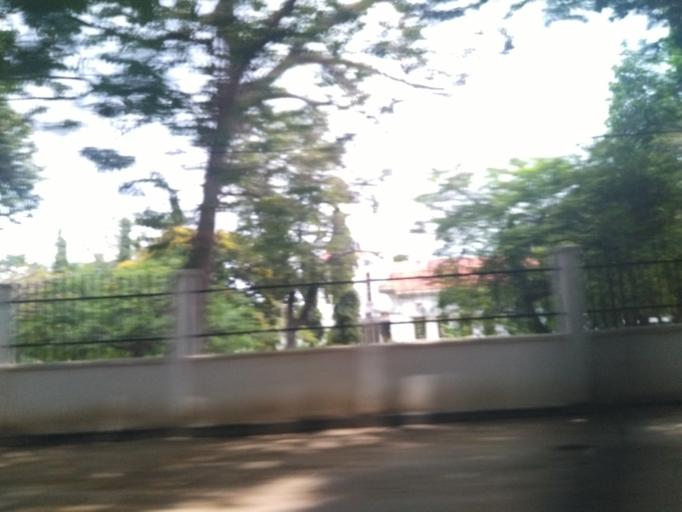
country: TZ
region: Dar es Salaam
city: Dar es Salaam
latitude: -6.8131
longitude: 39.2957
